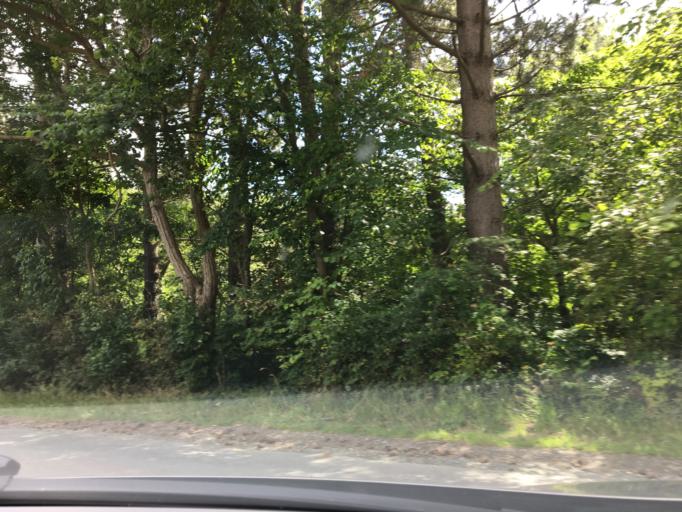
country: DK
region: South Denmark
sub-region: Svendborg Kommune
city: Svendborg
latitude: 55.0552
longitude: 10.5749
